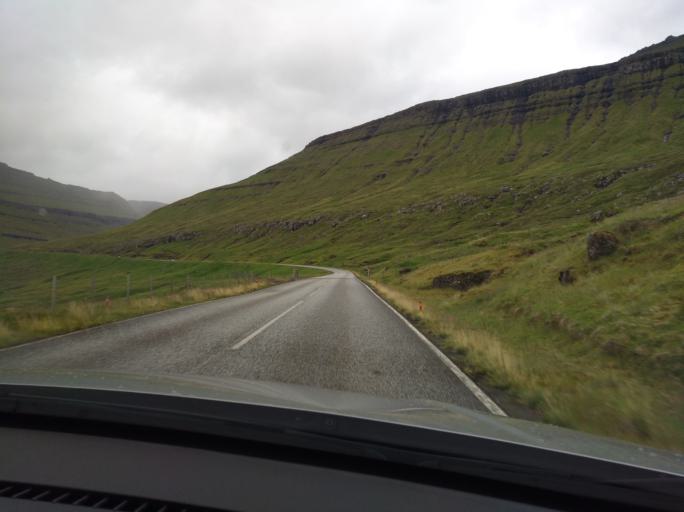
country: FO
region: Eysturoy
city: Fuglafjordur
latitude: 62.2144
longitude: -6.8633
